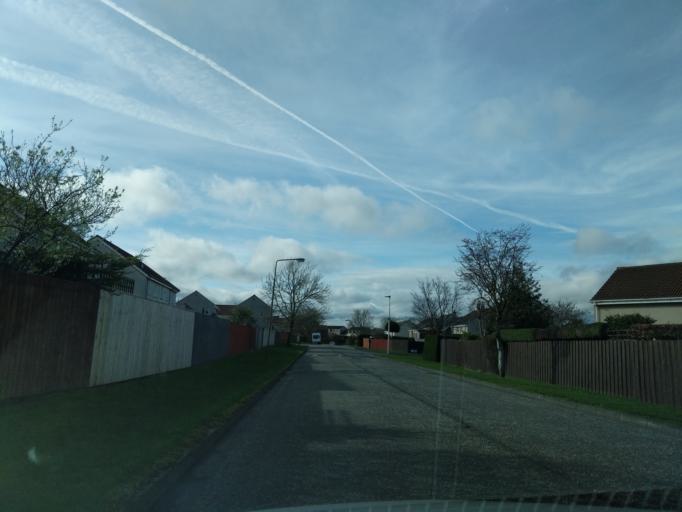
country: GB
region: Scotland
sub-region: Edinburgh
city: Queensferry
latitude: 55.9860
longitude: -3.4122
